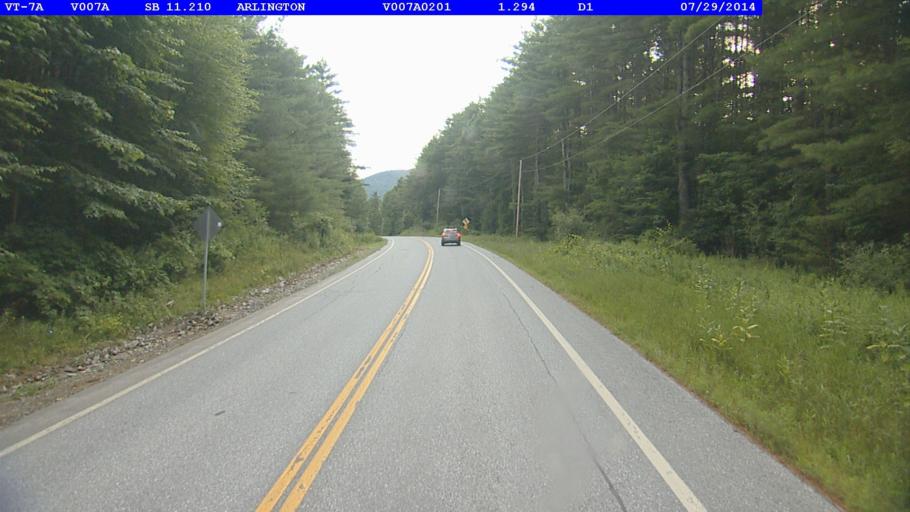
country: US
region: Vermont
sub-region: Bennington County
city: Arlington
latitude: 43.0409
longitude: -73.1714
